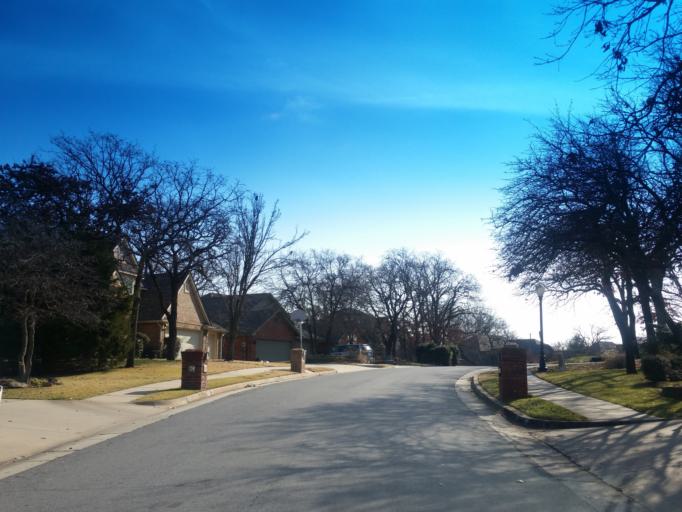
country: US
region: Oklahoma
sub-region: Oklahoma County
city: Edmond
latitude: 35.6453
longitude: -97.4327
